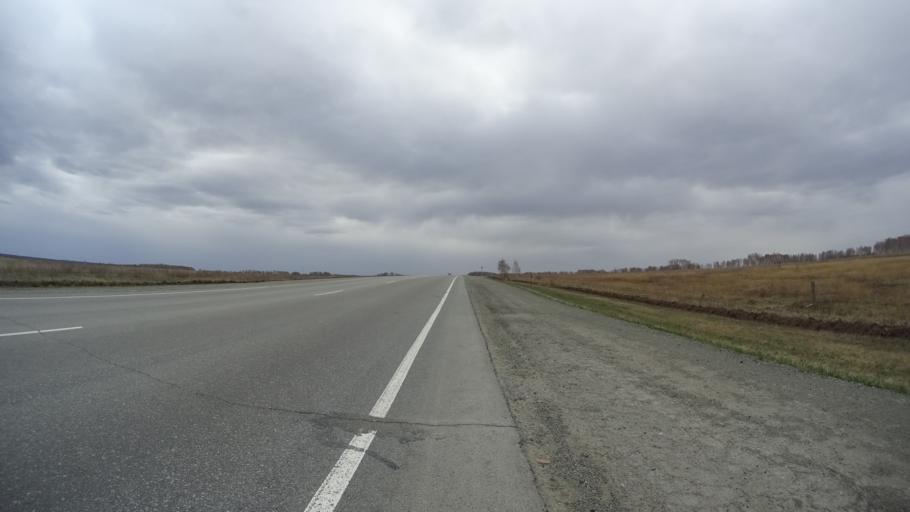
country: RU
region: Chelyabinsk
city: Yemanzhelinsk
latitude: 54.7077
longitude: 61.2578
